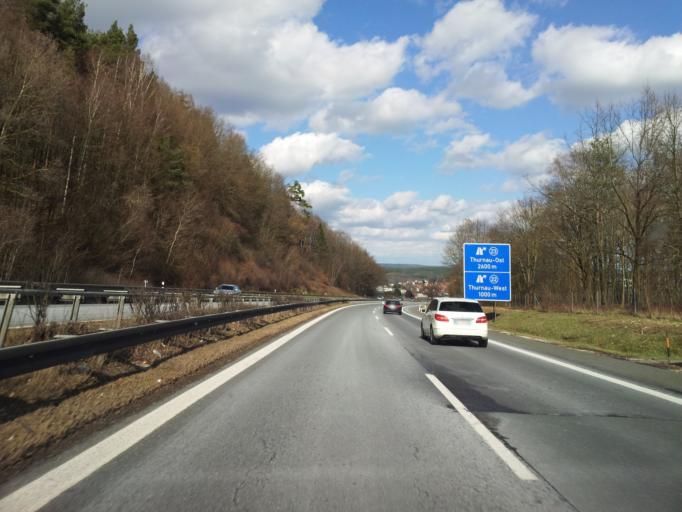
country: DE
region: Bavaria
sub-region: Upper Franconia
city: Thurnau
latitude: 50.0147
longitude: 11.3753
